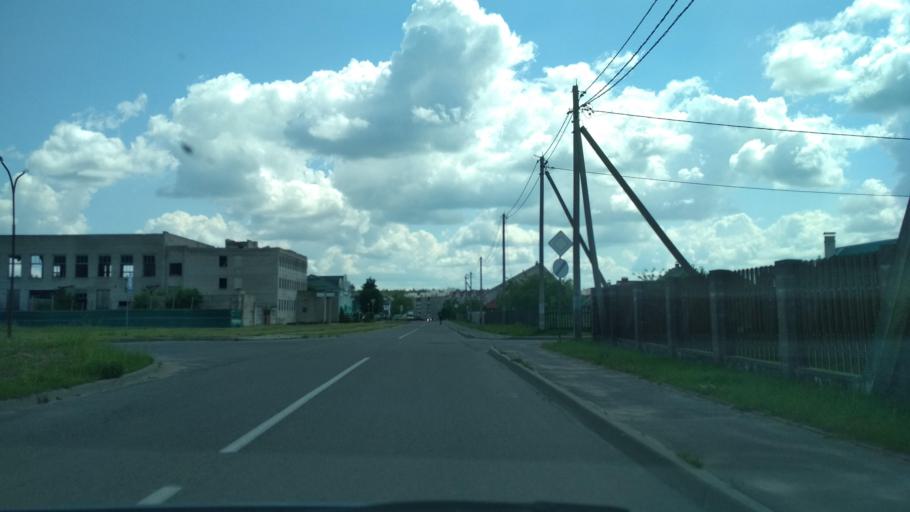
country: BY
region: Grodnenskaya
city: Astravyets
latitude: 54.6225
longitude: 25.9553
